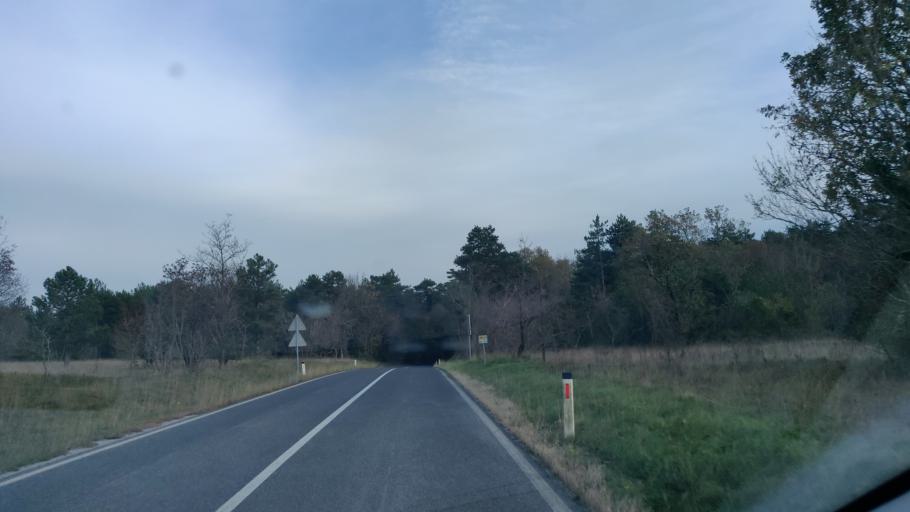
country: SI
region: Komen
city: Komen
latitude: 45.8197
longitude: 13.7595
